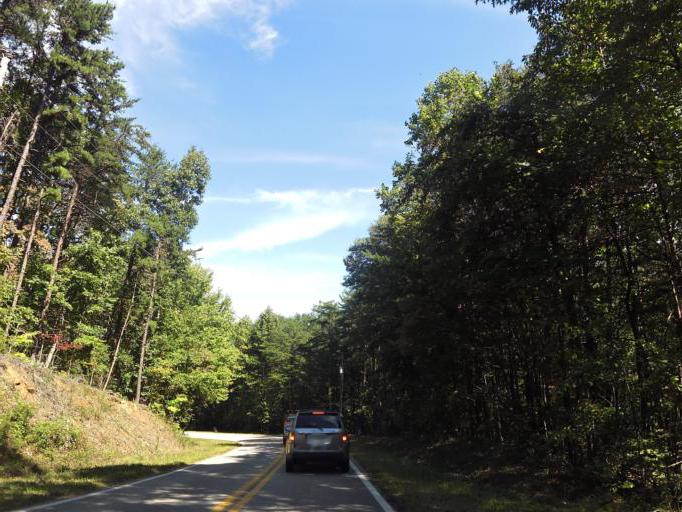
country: US
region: Georgia
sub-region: Pickens County
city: Nelson
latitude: 34.4857
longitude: -84.2590
